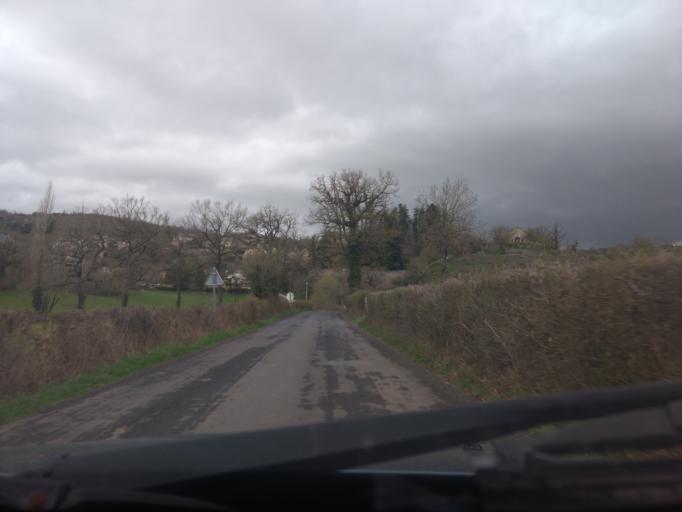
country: FR
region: Midi-Pyrenees
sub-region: Departement de l'Aveyron
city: La Loubiere
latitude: 44.3948
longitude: 2.6892
